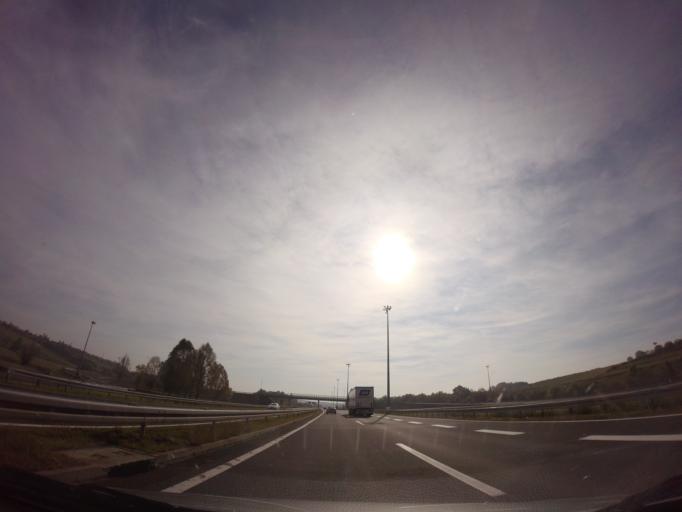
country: HR
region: Varazdinska
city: Remetinec
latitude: 46.1007
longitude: 16.2839
